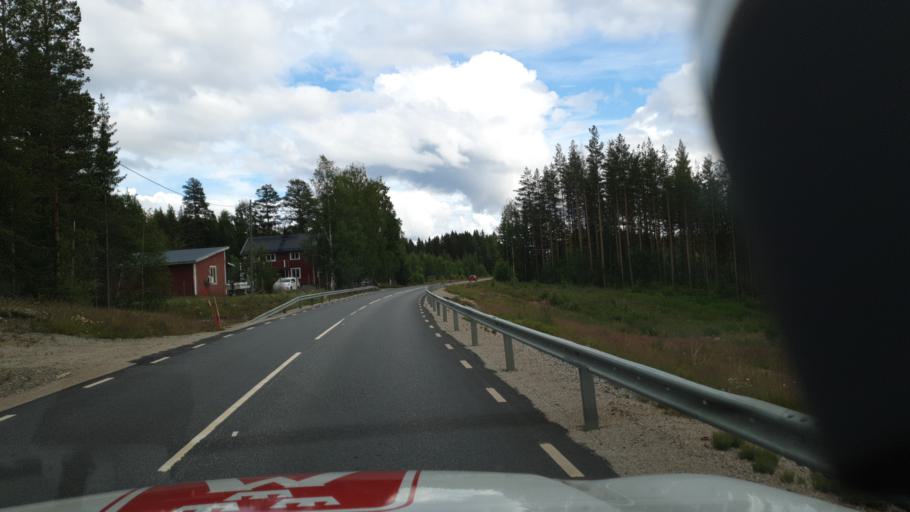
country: SE
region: Vaesterbotten
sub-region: Vindelns Kommun
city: Vindeln
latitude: 64.4056
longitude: 19.3105
